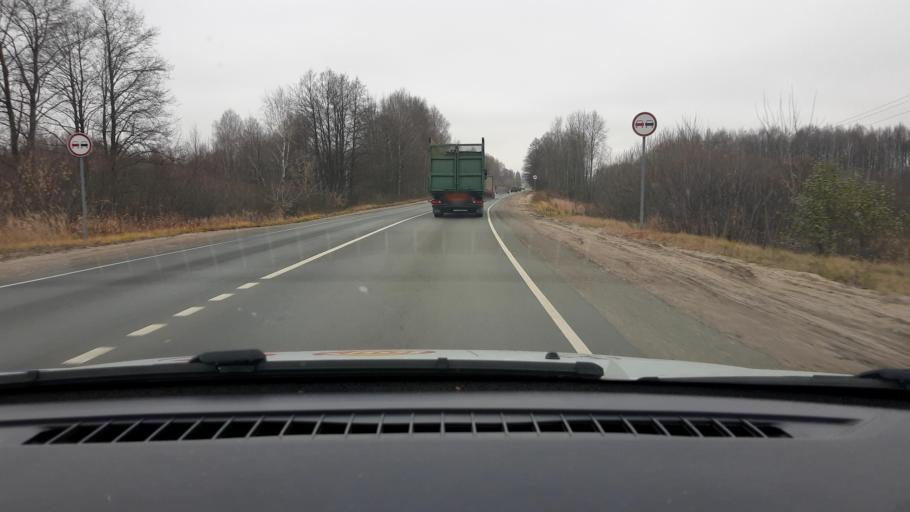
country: RU
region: Nizjnij Novgorod
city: Gorodets
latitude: 56.5687
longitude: 43.4824
